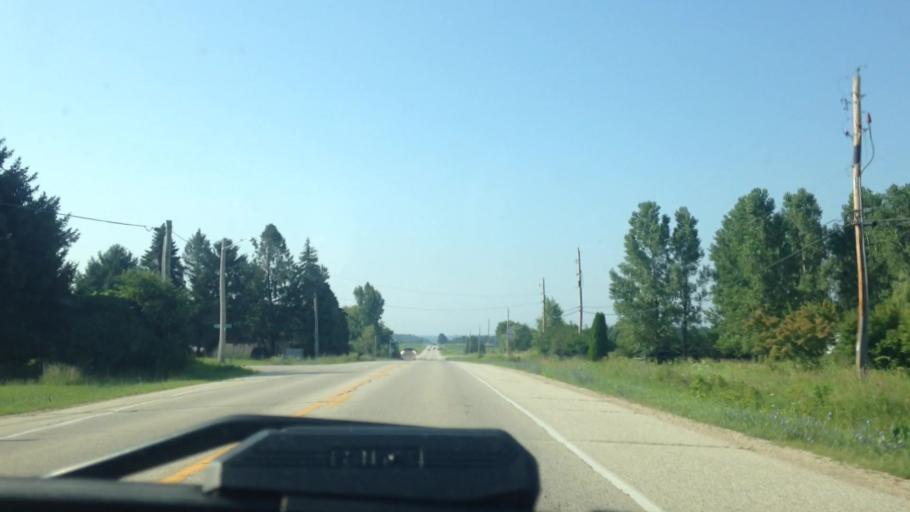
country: US
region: Wisconsin
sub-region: Washington County
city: Richfield
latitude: 43.2290
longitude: -88.2619
